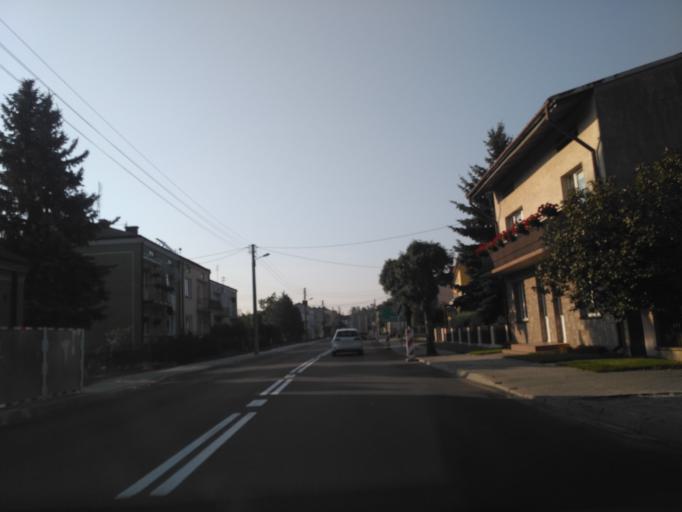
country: PL
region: Lublin Voivodeship
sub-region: Powiat janowski
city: Modliborzyce
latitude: 50.7558
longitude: 22.3284
